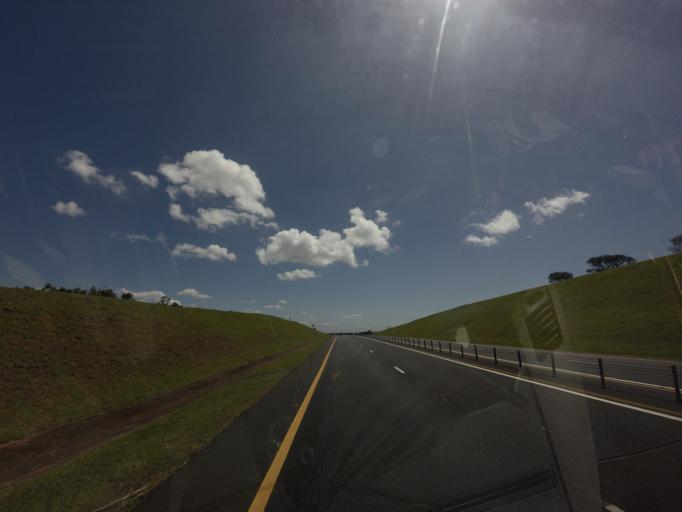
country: ZA
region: KwaZulu-Natal
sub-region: iLembe District Municipality
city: Mandeni
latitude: -29.0624
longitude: 31.6257
